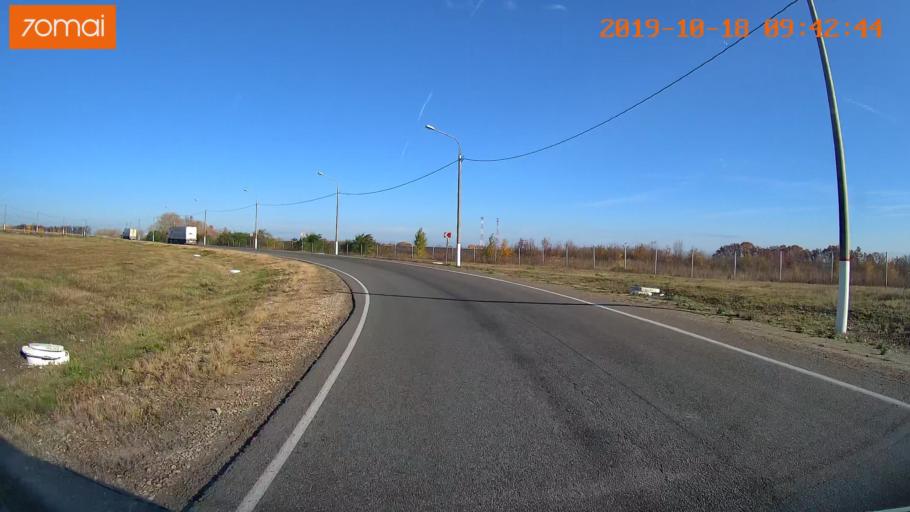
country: RU
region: Tula
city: Kazachka
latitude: 53.2892
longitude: 38.1803
